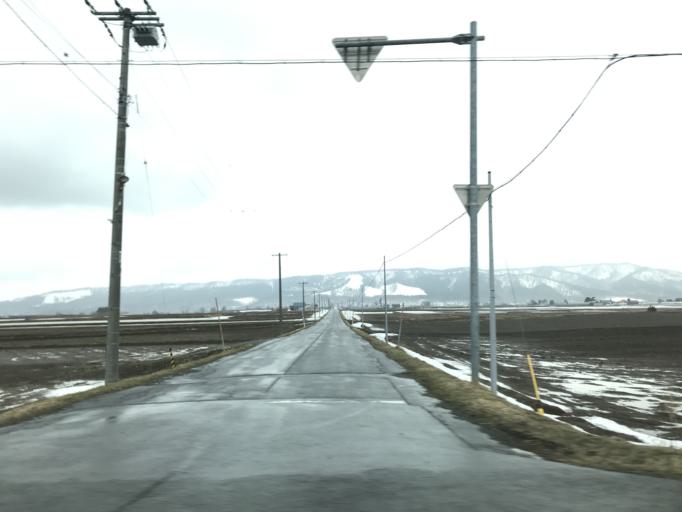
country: JP
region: Hokkaido
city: Nayoro
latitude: 44.2259
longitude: 142.3948
